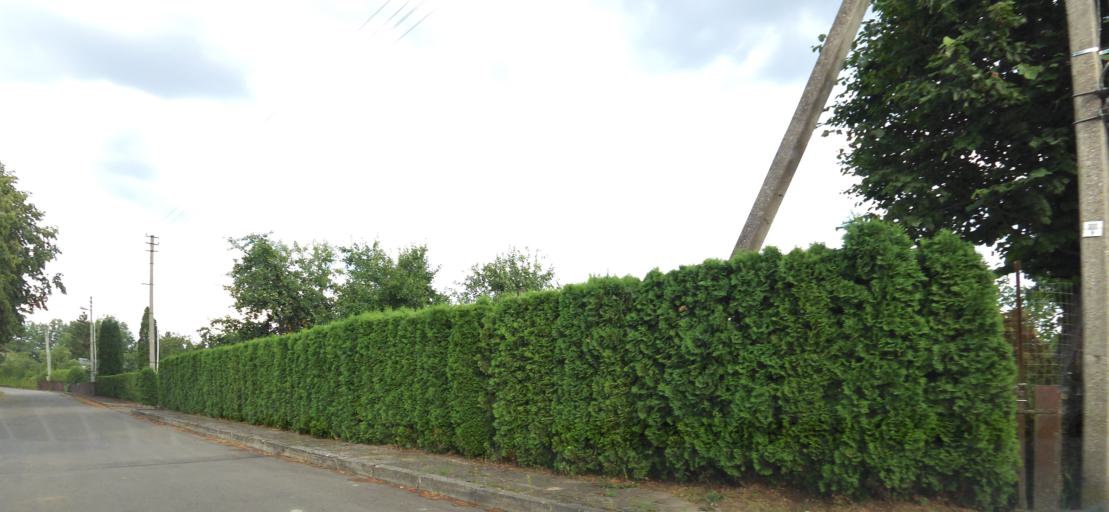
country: LT
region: Alytaus apskritis
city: Varena
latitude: 54.2134
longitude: 24.4182
